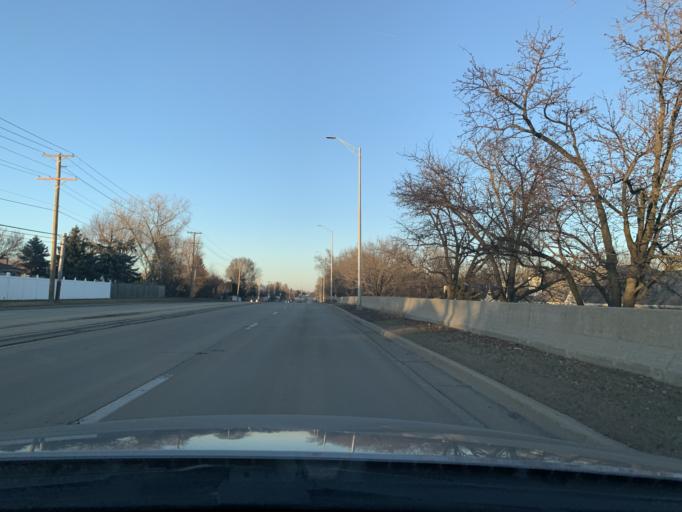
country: US
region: Illinois
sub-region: Cook County
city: Schaumburg
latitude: 42.0196
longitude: -88.0604
